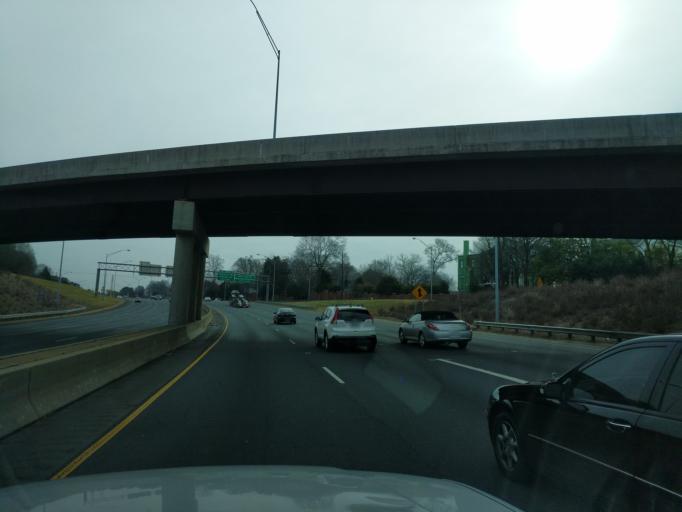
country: US
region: North Carolina
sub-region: Mecklenburg County
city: Charlotte
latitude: 35.2196
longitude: -80.8254
